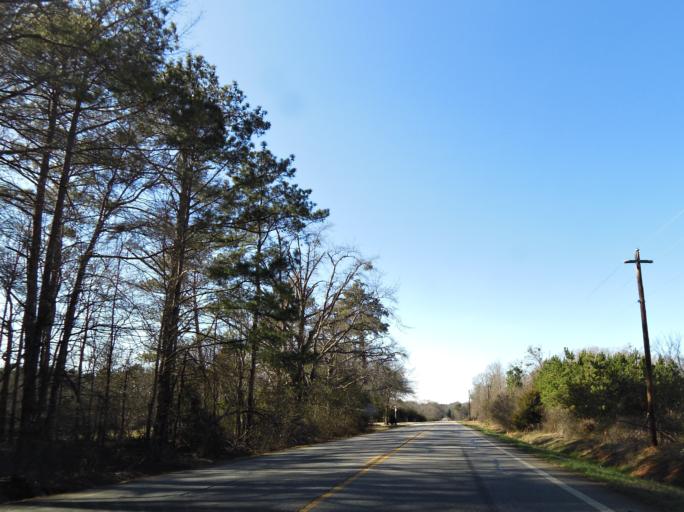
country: US
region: Georgia
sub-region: Lamar County
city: Barnesville
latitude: 32.9135
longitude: -84.1651
